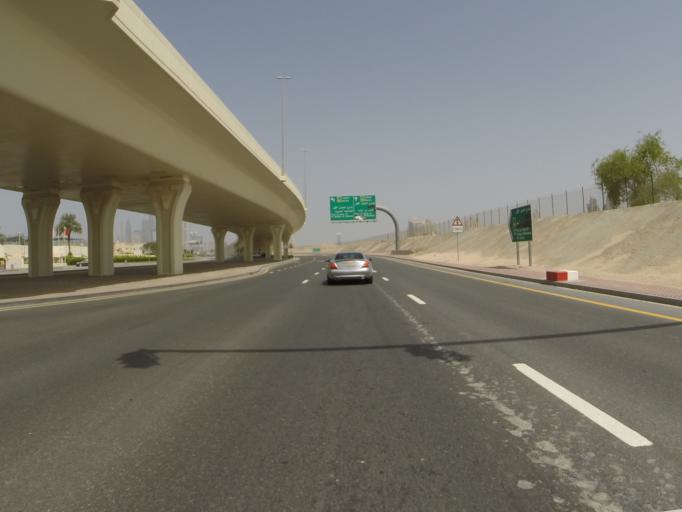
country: AE
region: Dubai
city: Dubai
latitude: 25.0785
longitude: 55.1803
